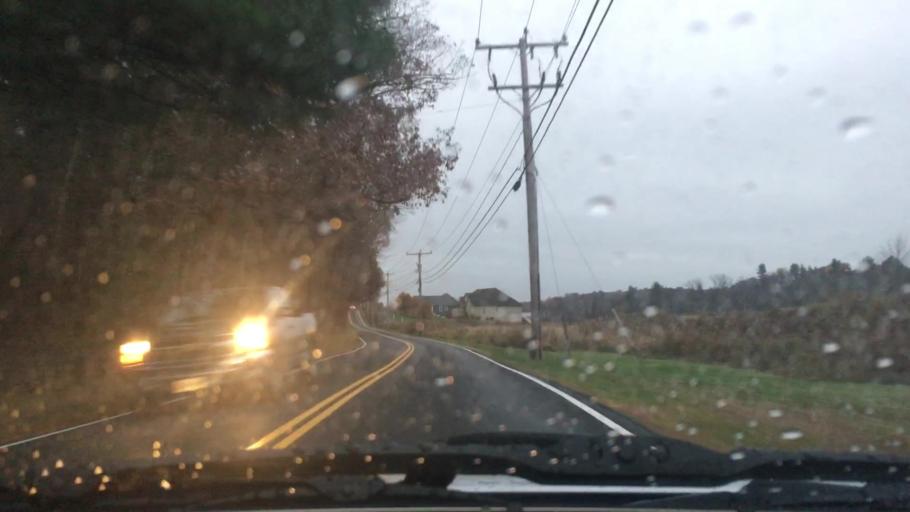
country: US
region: Massachusetts
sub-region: Hampden County
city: Southwick
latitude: 42.0856
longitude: -72.7742
